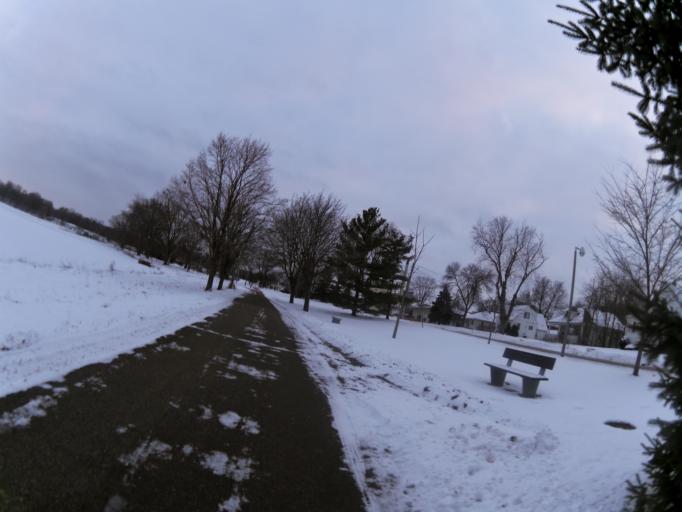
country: US
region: Minnesota
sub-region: Olmsted County
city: Rochester
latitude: 44.0332
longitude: -92.4593
